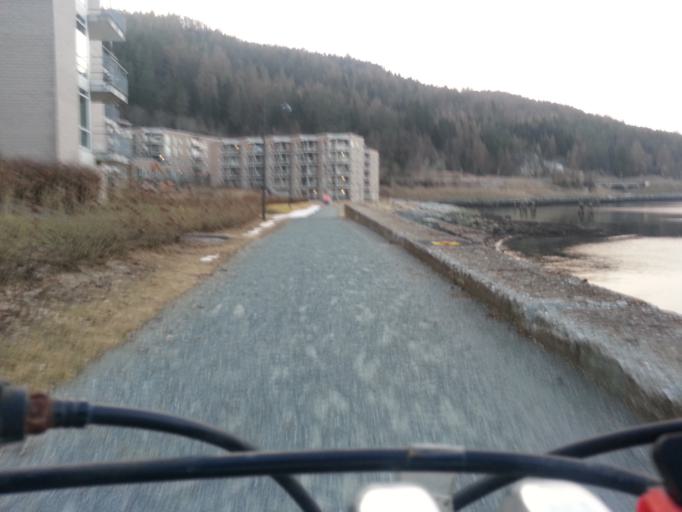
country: NO
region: Sor-Trondelag
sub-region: Trondheim
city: Trondheim
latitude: 63.4326
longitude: 10.3551
